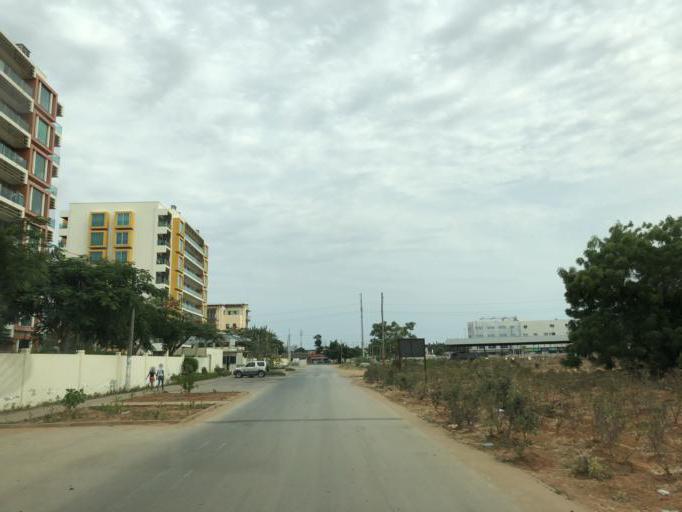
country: AO
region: Luanda
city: Luanda
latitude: -8.8927
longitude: 13.1928
